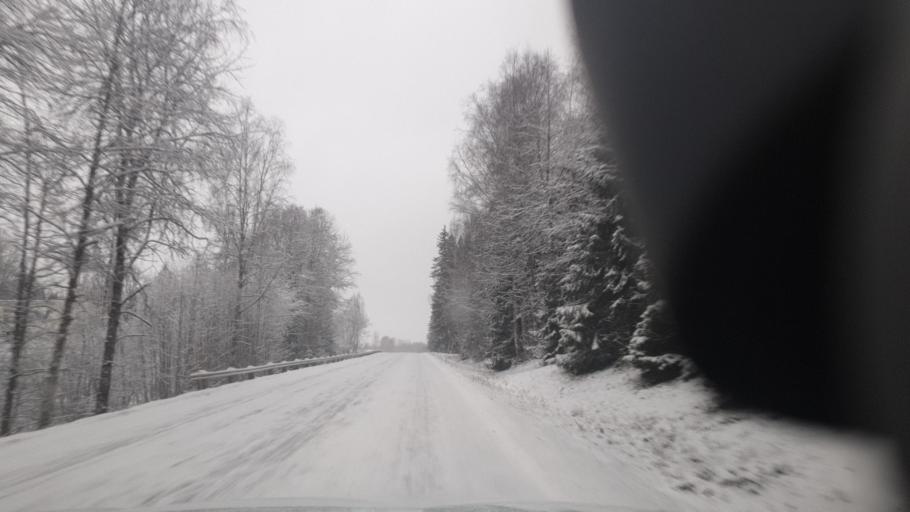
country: SE
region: Vaermland
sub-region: Eda Kommun
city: Charlottenberg
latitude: 59.7988
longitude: 12.1542
